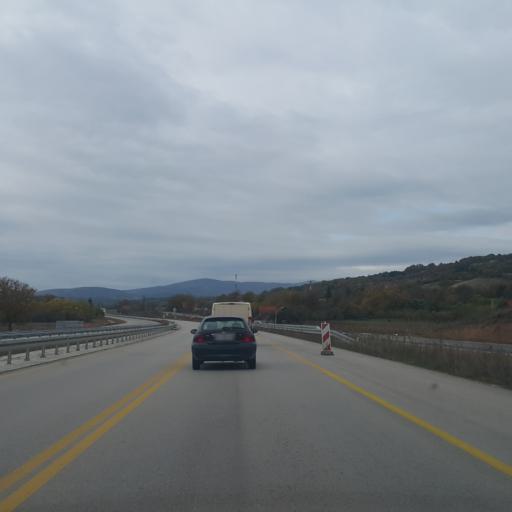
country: RS
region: Central Serbia
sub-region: Pirotski Okrug
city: Pirot
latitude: 43.2198
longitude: 22.4968
